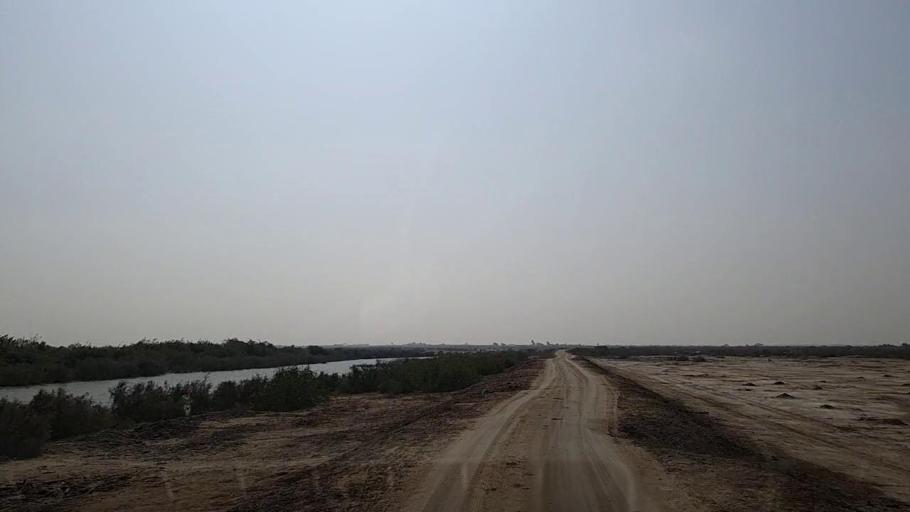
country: PK
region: Sindh
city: Gharo
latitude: 24.6783
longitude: 67.7337
